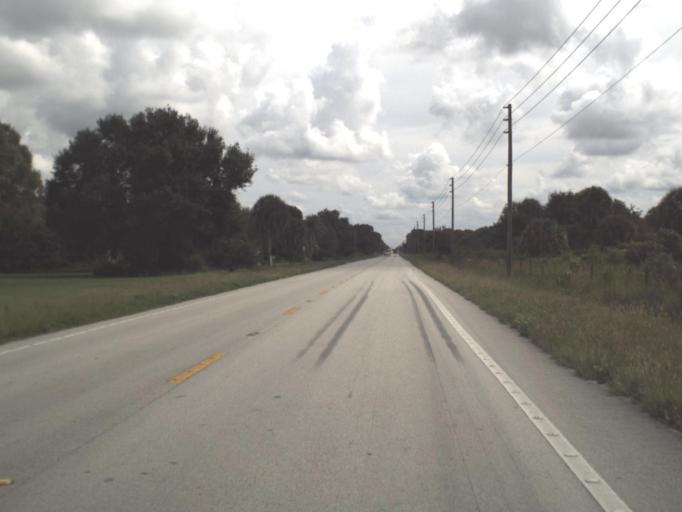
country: US
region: Florida
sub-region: Okeechobee County
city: Okeechobee
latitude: 27.2435
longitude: -80.8693
